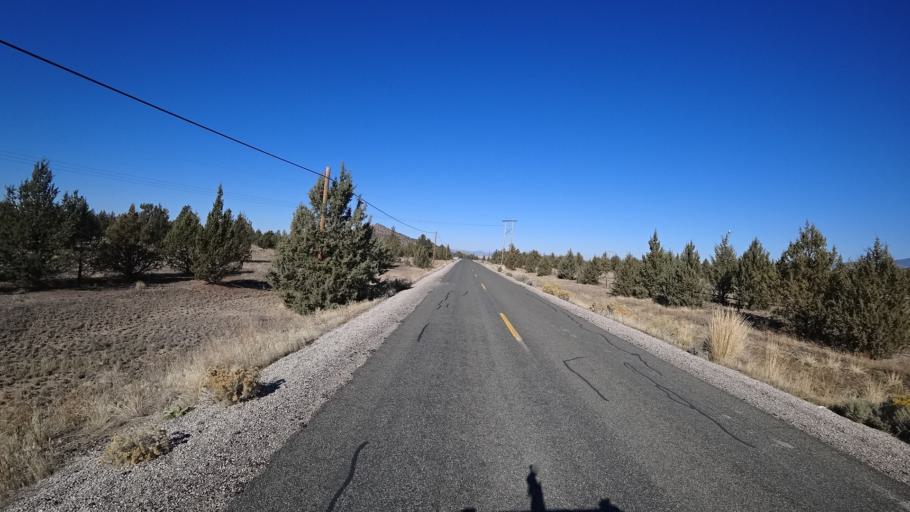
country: US
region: California
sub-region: Siskiyou County
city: Montague
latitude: 41.6545
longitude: -122.3626
